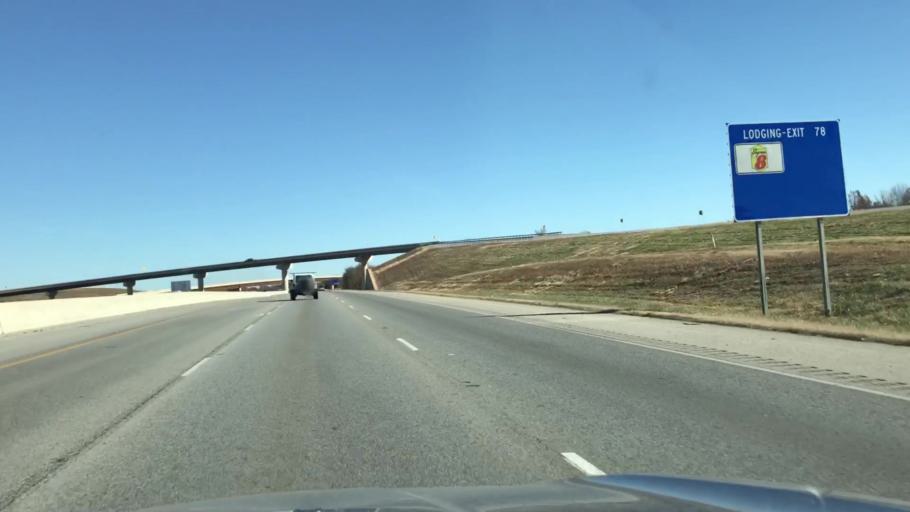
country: US
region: Arkansas
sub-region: Benton County
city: Lowell
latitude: 36.2360
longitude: -94.1644
